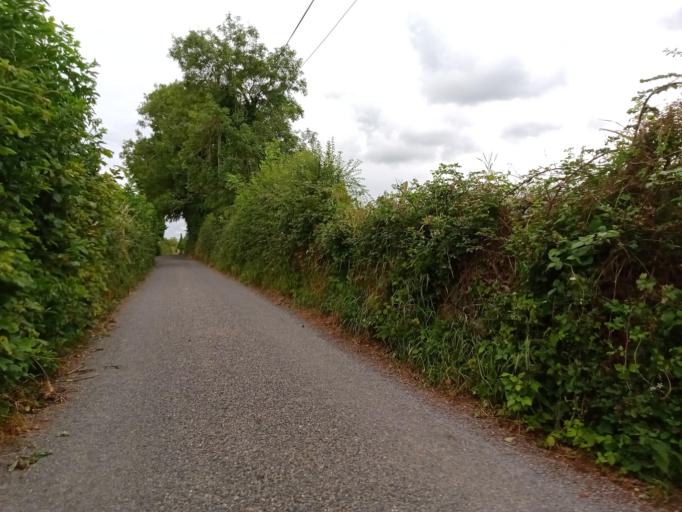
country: IE
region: Leinster
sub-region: Kilkenny
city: Callan
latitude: 52.5446
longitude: -7.4126
